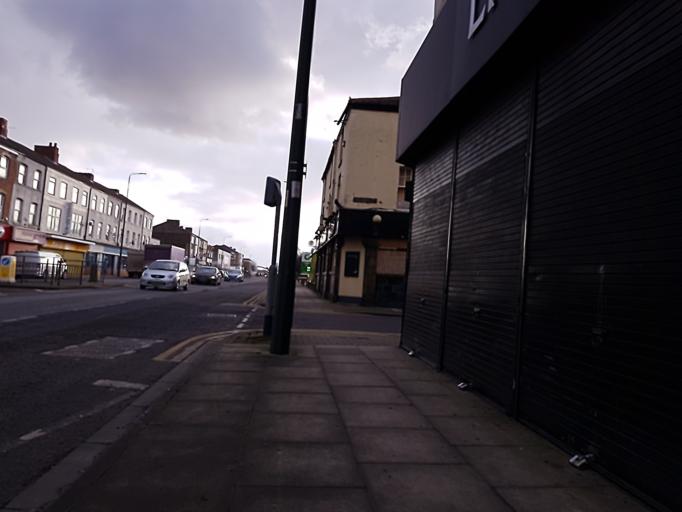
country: GB
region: England
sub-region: North East Lincolnshire
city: Grimsby
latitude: 53.5746
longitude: -0.0695
